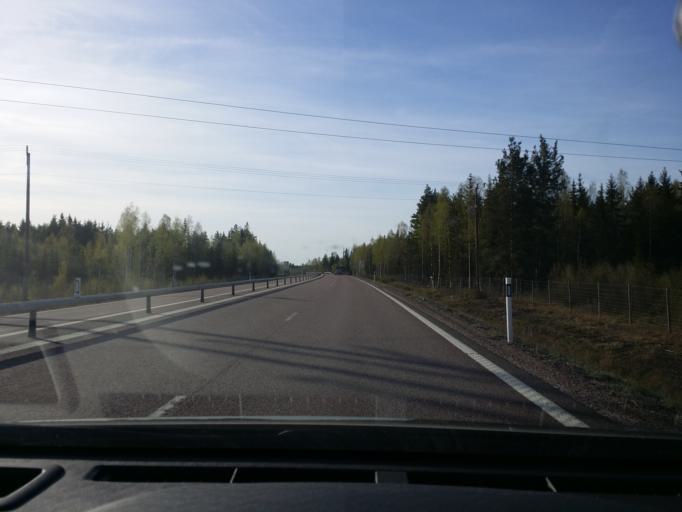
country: SE
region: Dalarna
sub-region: Avesta Kommun
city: Avesta
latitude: 60.1318
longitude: 16.2716
